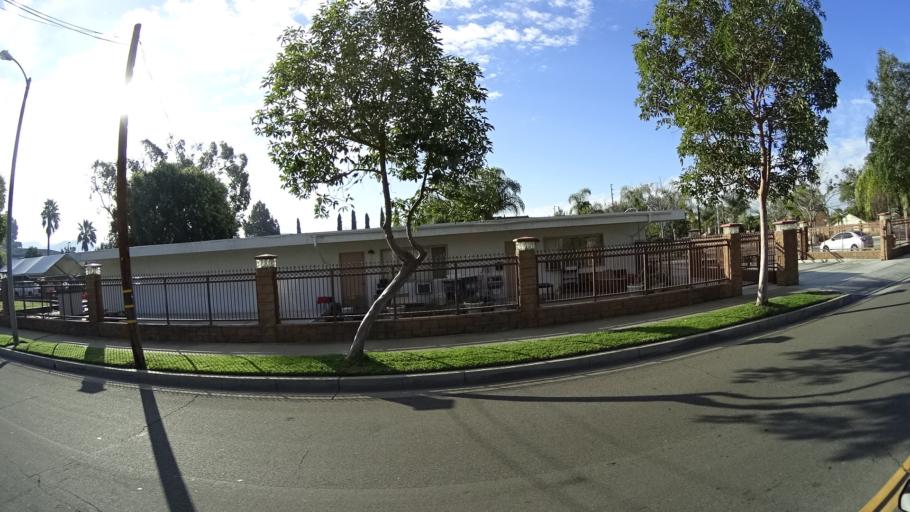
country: US
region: California
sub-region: Orange County
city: Villa Park
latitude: 33.7950
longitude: -117.8049
